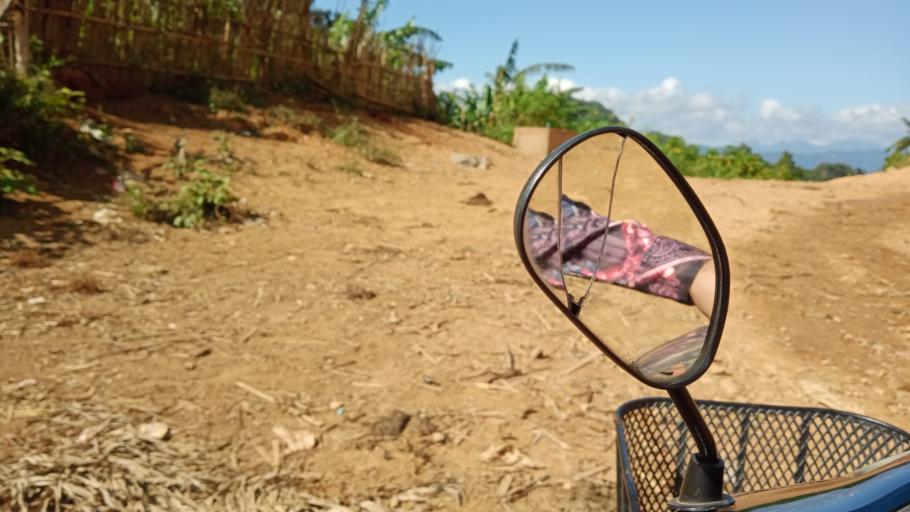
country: LA
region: Xiangkhoang
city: Phonsavan
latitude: 19.1178
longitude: 102.9162
